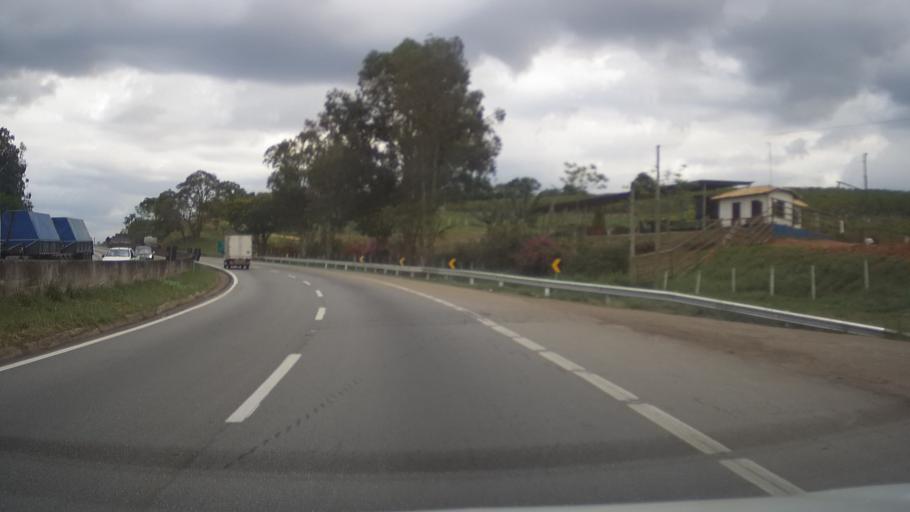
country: BR
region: Minas Gerais
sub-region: Tres Coracoes
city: Tres Coracoes
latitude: -21.4786
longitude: -45.2011
